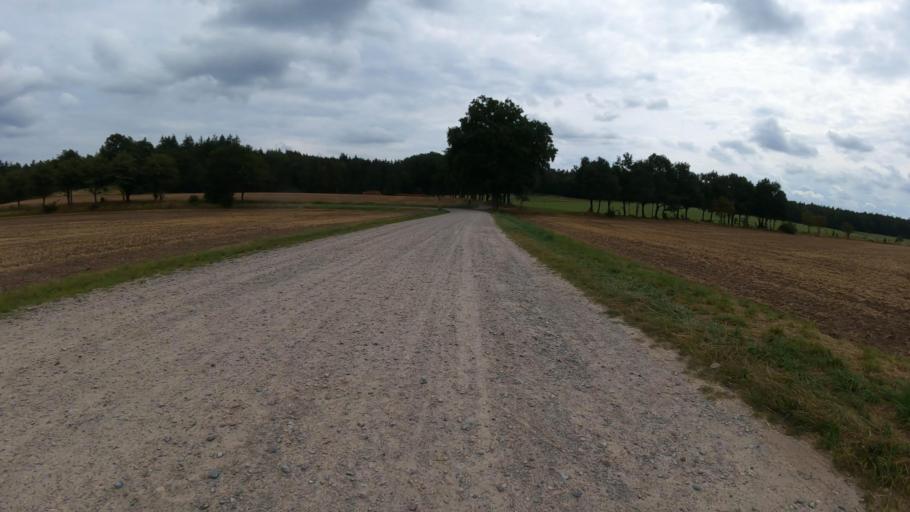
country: DE
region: Lower Saxony
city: Bendestorf
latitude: 53.3465
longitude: 9.9162
